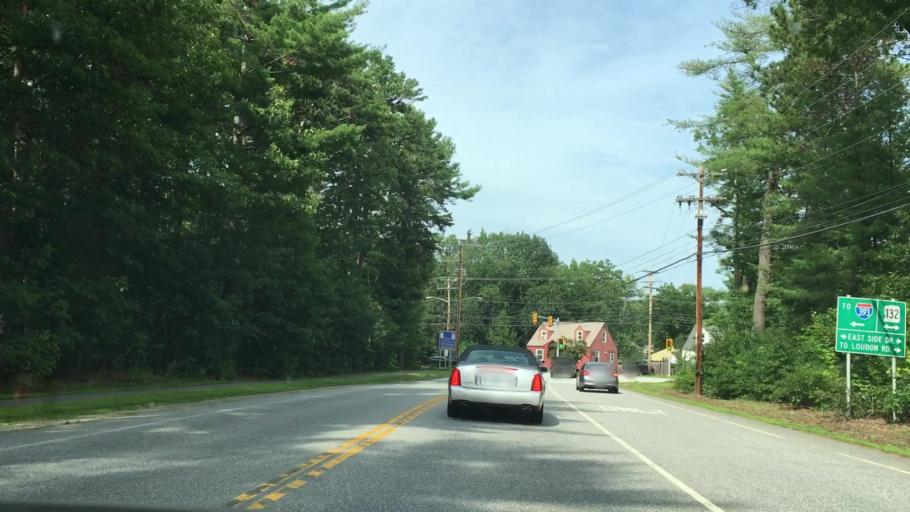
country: US
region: New Hampshire
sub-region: Merrimack County
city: Concord
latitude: 43.2215
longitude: -71.5079
